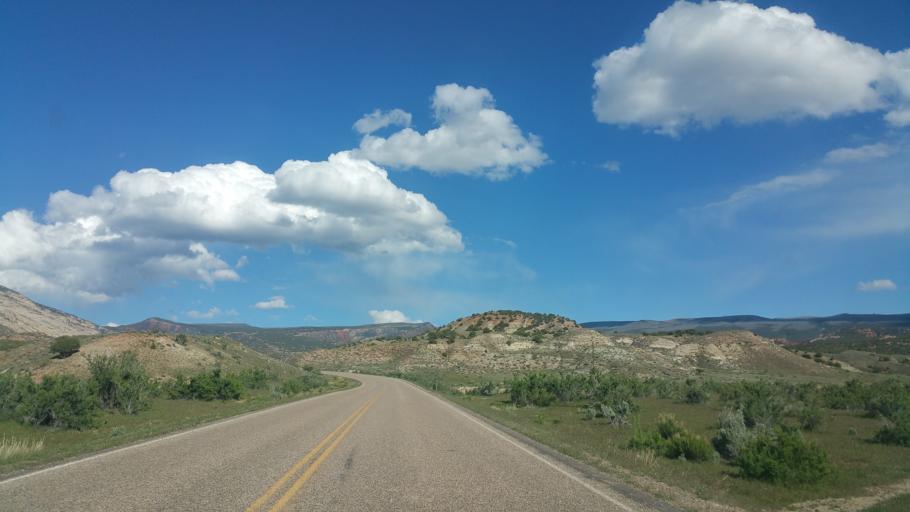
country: US
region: Utah
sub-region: Uintah County
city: Naples
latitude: 40.4239
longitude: -109.2219
